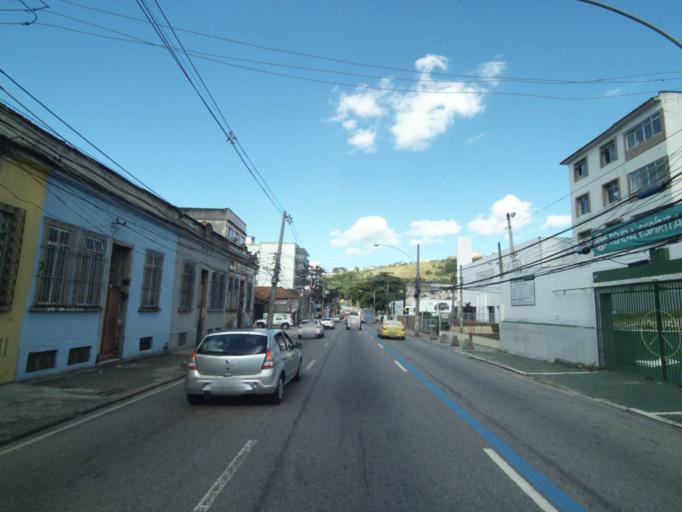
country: BR
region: Rio de Janeiro
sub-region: Rio De Janeiro
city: Rio de Janeiro
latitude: -22.9038
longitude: -43.2452
